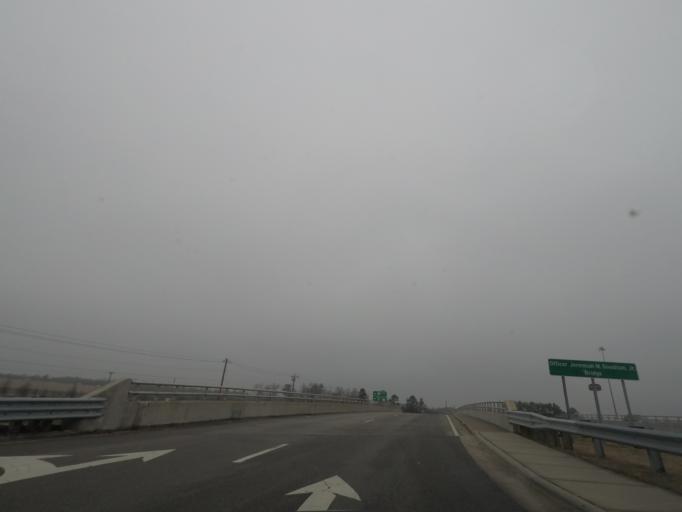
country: US
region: North Carolina
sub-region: Robeson County
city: Lumberton
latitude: 34.6696
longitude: -79.0056
